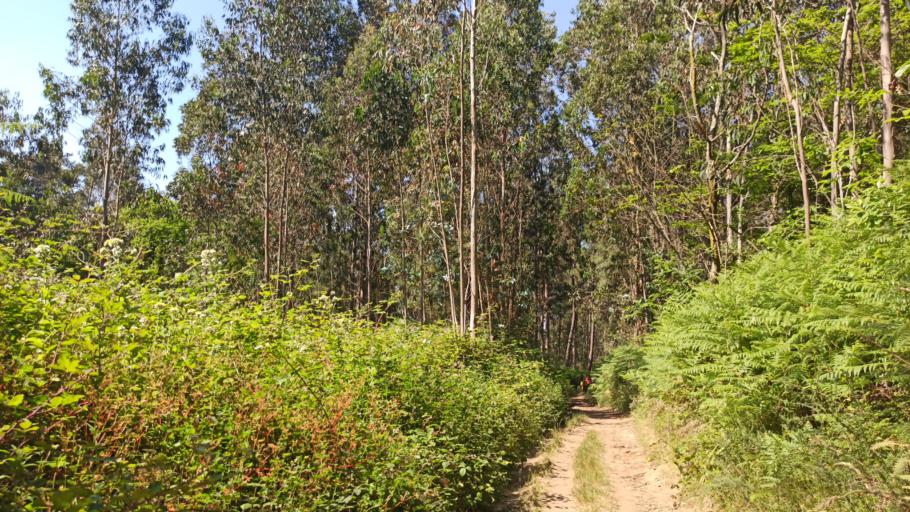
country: ES
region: Galicia
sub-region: Provincia da Coruna
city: Sada
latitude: 43.3812
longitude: -8.2713
